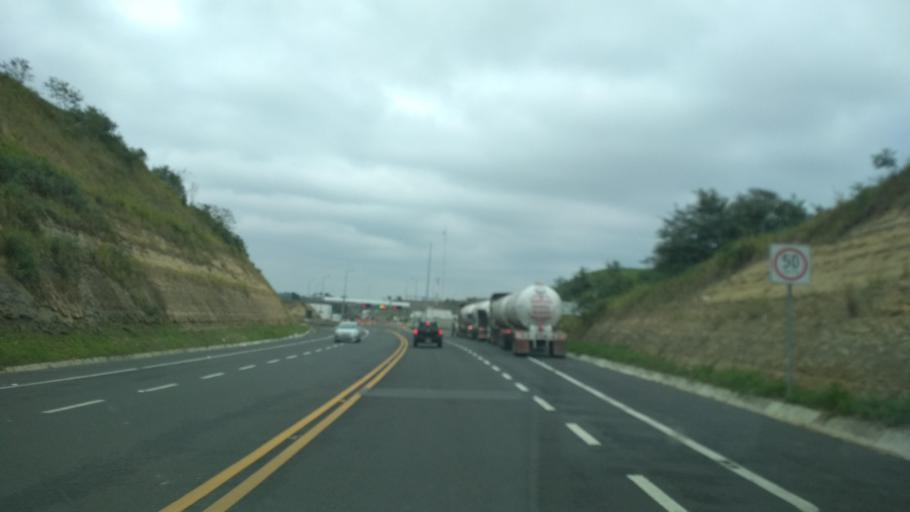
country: MX
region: Veracruz
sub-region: Papantla
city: Polutla
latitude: 20.4574
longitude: -97.2448
